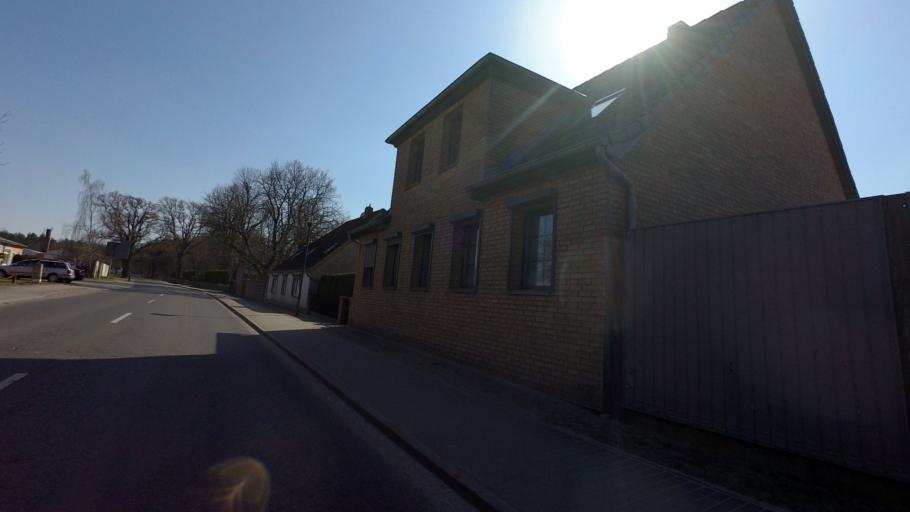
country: DE
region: Brandenburg
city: Leegebruch
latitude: 52.7484
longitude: 13.1721
